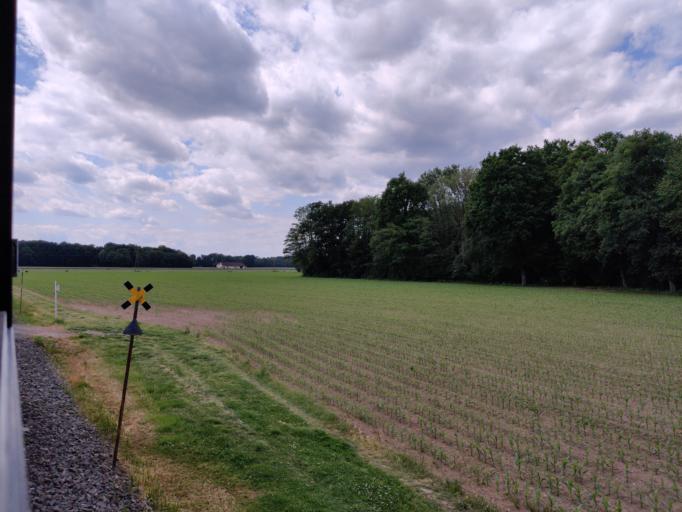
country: AT
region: Styria
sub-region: Politischer Bezirk Suedoststeiermark
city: Eichfeld
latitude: 46.7143
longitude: 15.7403
